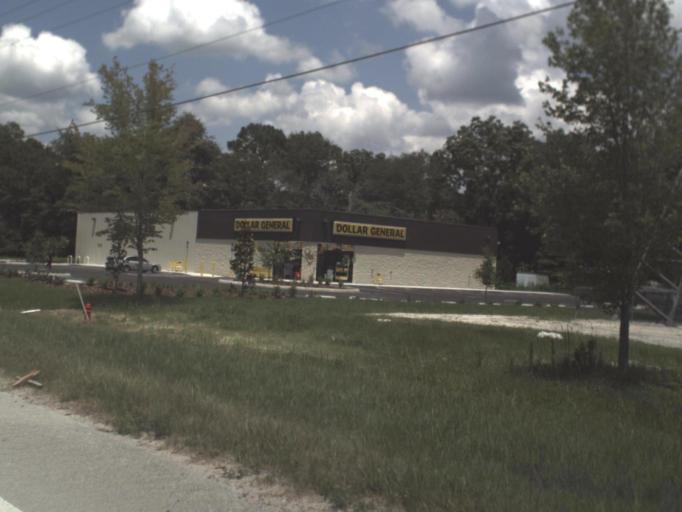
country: US
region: Florida
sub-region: Baker County
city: Macclenny
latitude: 30.2509
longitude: -82.1240
